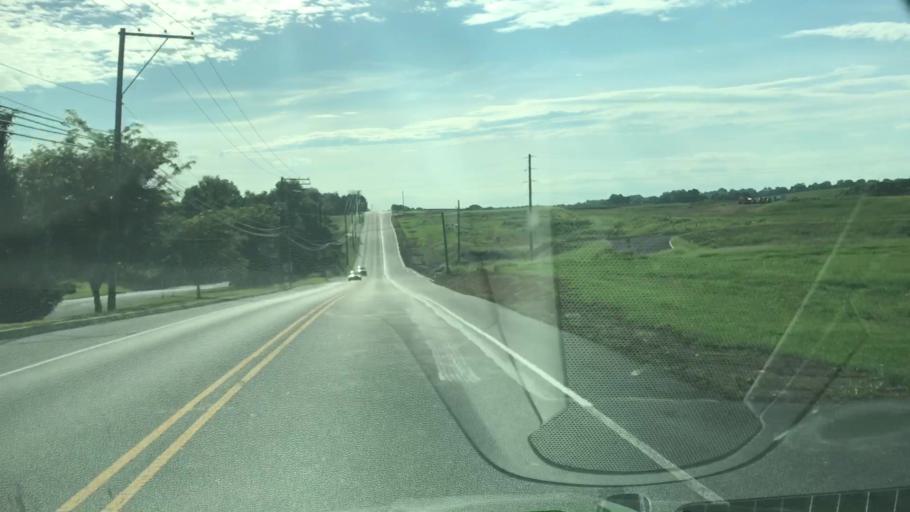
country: US
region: Pennsylvania
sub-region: Dauphin County
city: Highspire
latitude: 40.2272
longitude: -76.7661
